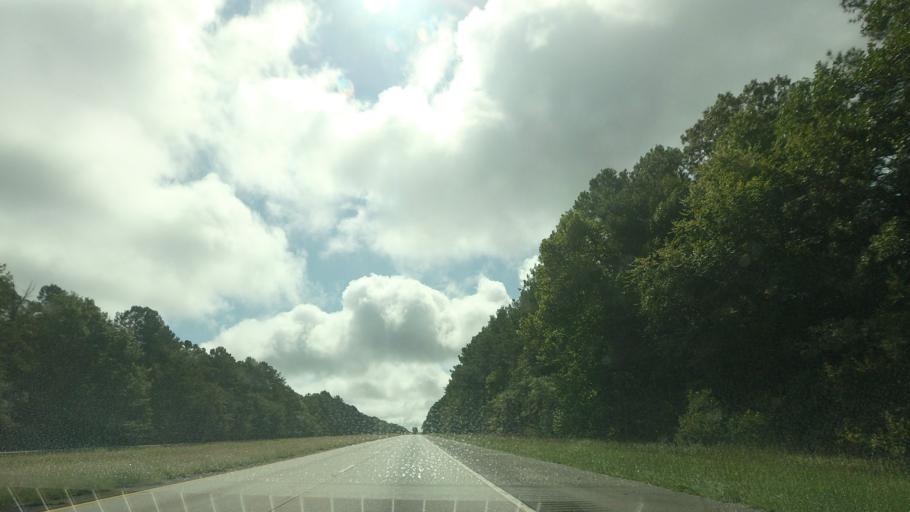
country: US
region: Georgia
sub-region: Twiggs County
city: Jeffersonville
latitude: 32.6376
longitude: -83.3970
